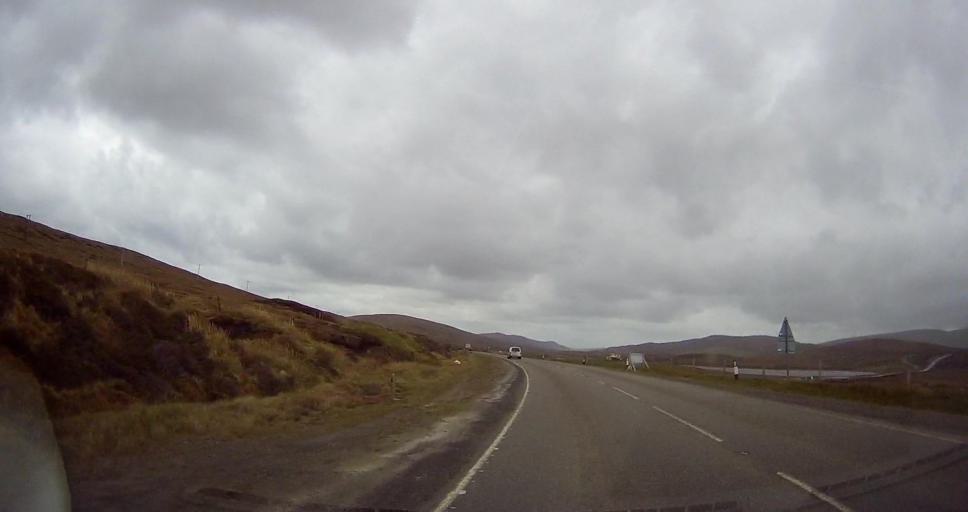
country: GB
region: Scotland
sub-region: Shetland Islands
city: Lerwick
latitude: 60.2846
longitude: -1.2432
